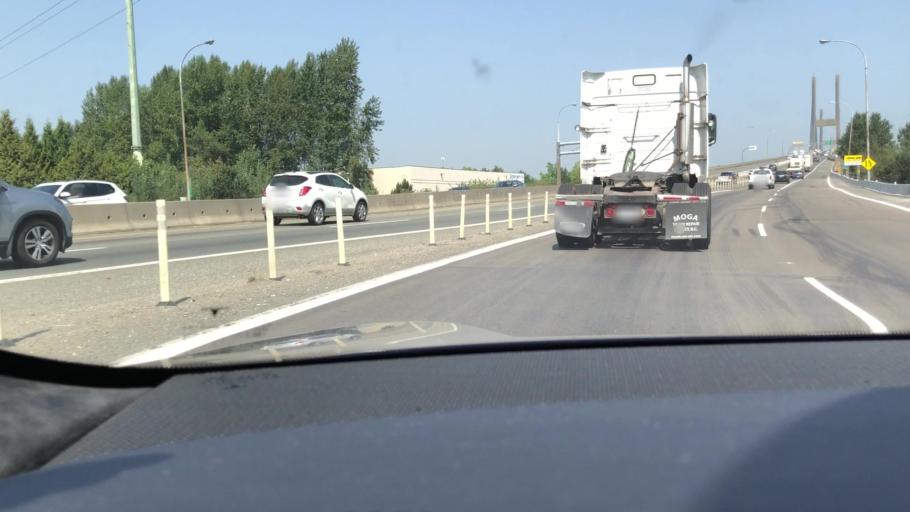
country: CA
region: British Columbia
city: Delta
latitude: 49.1472
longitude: -122.9374
